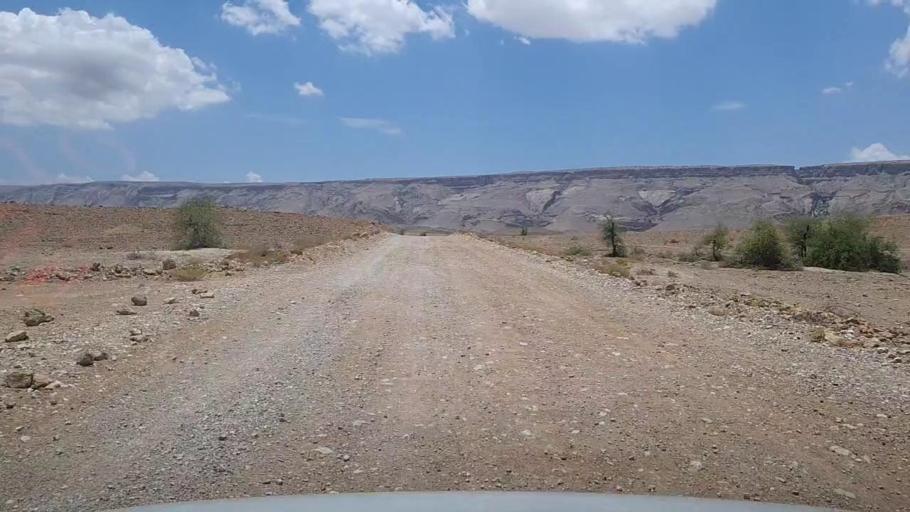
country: PK
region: Sindh
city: Bhan
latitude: 26.2658
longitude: 67.5151
